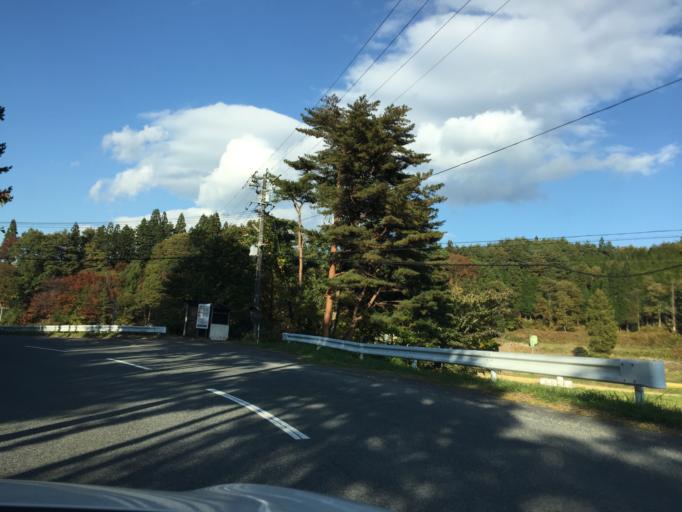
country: JP
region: Fukushima
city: Iwaki
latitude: 37.2600
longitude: 140.7653
